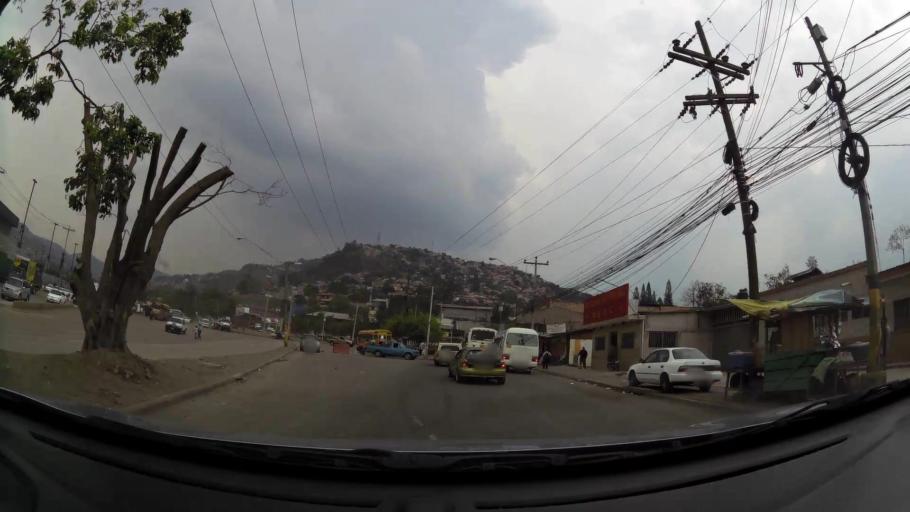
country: HN
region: Francisco Morazan
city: Tegucigalpa
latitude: 14.1046
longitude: -87.2323
